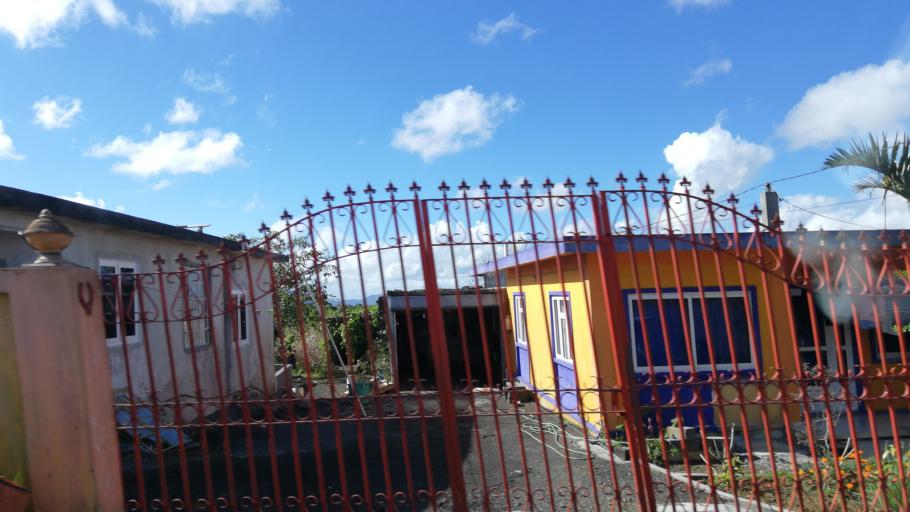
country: MU
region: Moka
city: Quartier Militaire
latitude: -20.2305
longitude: 57.5974
